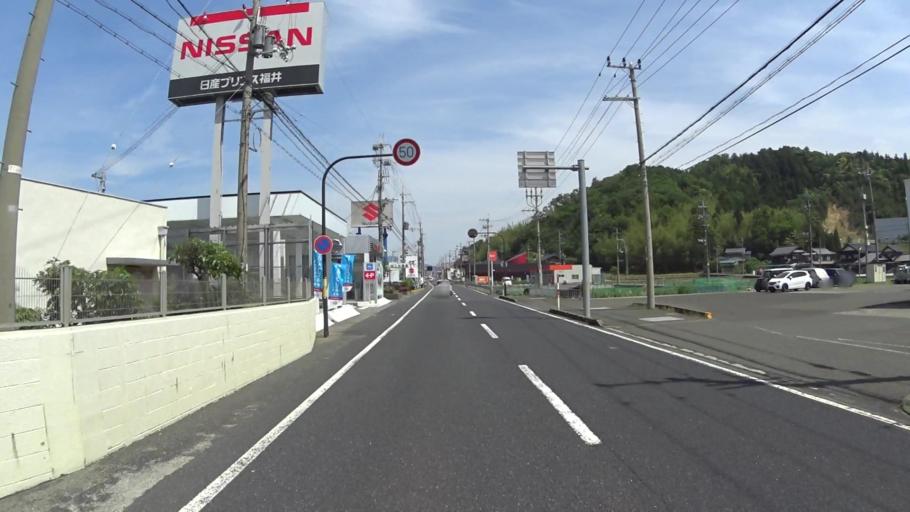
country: JP
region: Fukui
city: Obama
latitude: 35.4856
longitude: 135.7681
